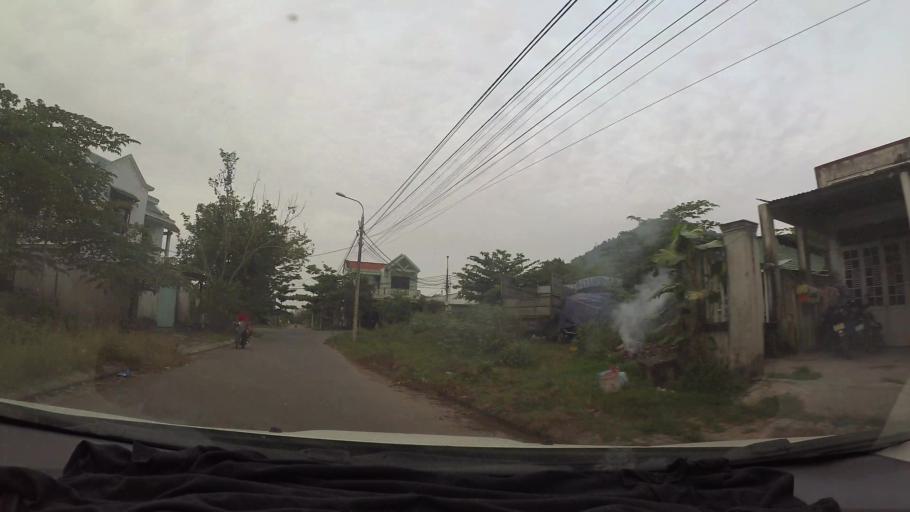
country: VN
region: Da Nang
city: Lien Chieu
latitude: 16.0665
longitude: 108.1043
